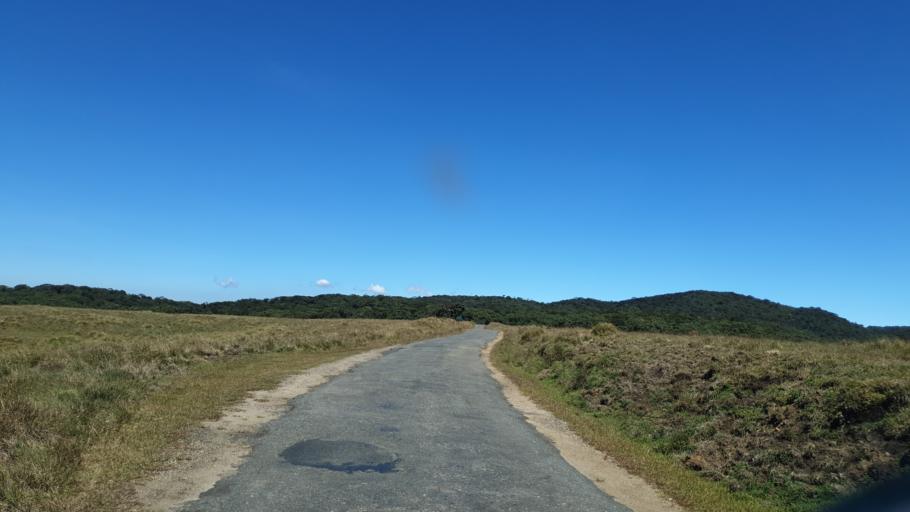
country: LK
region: Central
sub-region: Nuwara Eliya District
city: Nuwara Eliya
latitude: 6.8222
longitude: 80.8057
